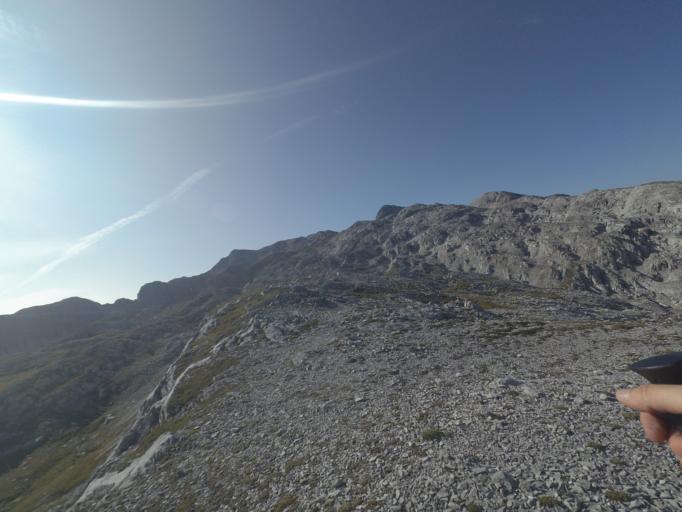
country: AT
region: Salzburg
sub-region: Politischer Bezirk Sankt Johann im Pongau
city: Kleinarl
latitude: 47.2208
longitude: 13.4051
